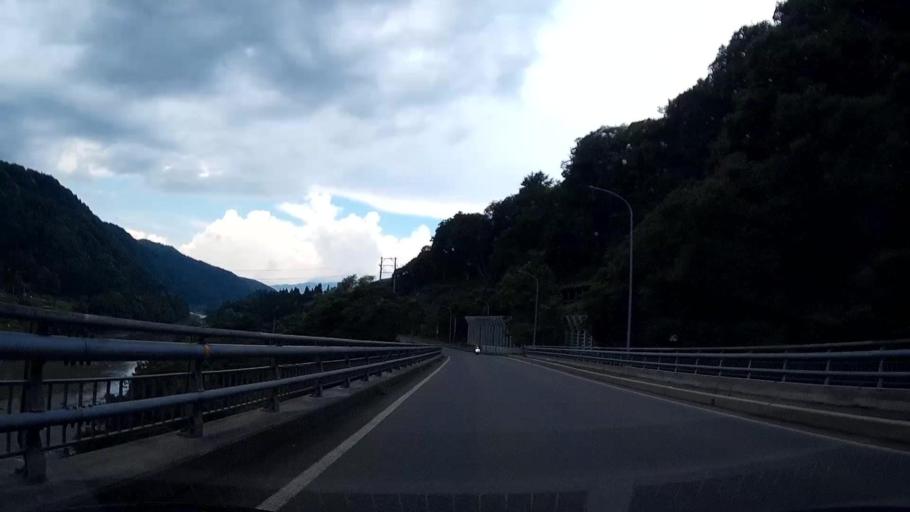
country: JP
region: Nagano
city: Iiyama
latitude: 36.9851
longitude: 138.5169
